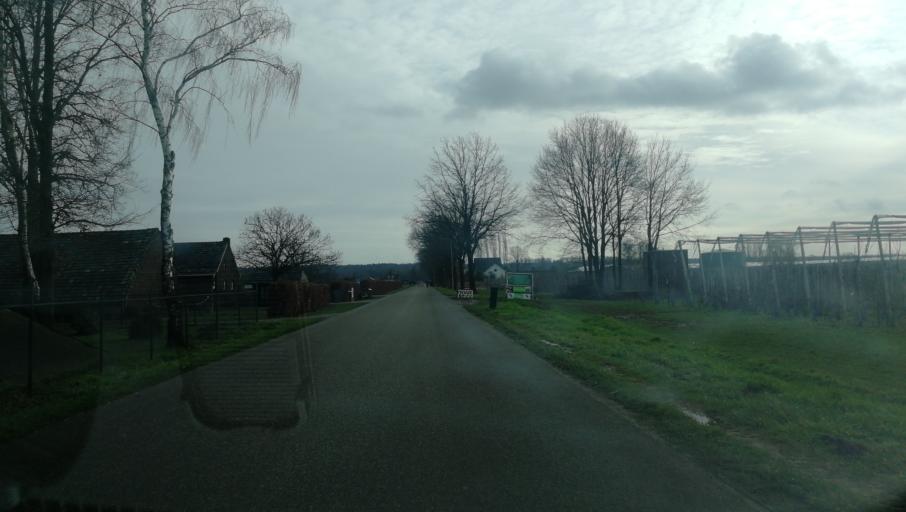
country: NL
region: Limburg
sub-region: Gemeente Beesel
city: Offenbeek
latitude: 51.3039
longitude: 6.1232
